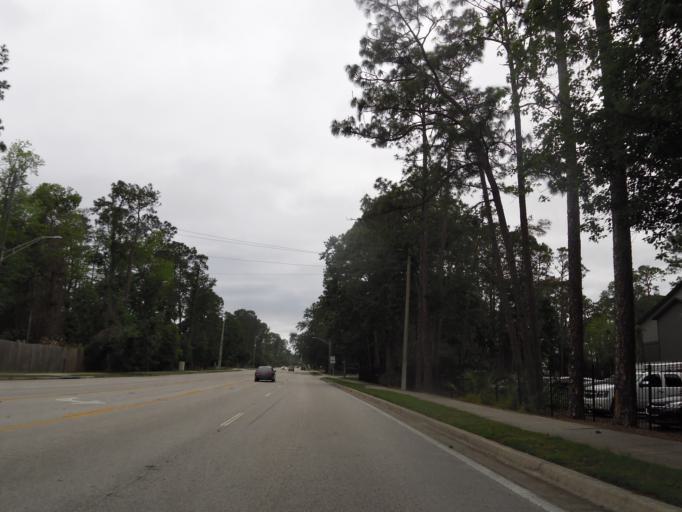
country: US
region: Florida
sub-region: Saint Johns County
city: Fruit Cove
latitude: 30.1909
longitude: -81.6084
